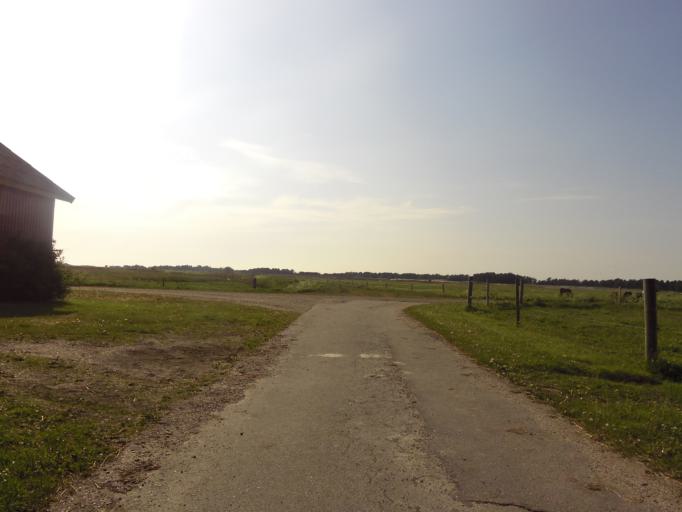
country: DE
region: Schleswig-Holstein
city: List
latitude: 55.1749
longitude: 8.5547
